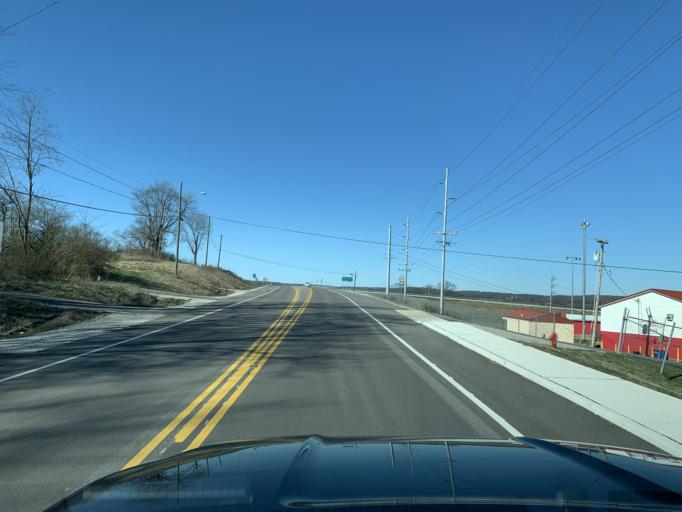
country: US
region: Tennessee
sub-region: Maury County
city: Mount Pleasant
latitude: 35.5428
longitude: -87.2174
